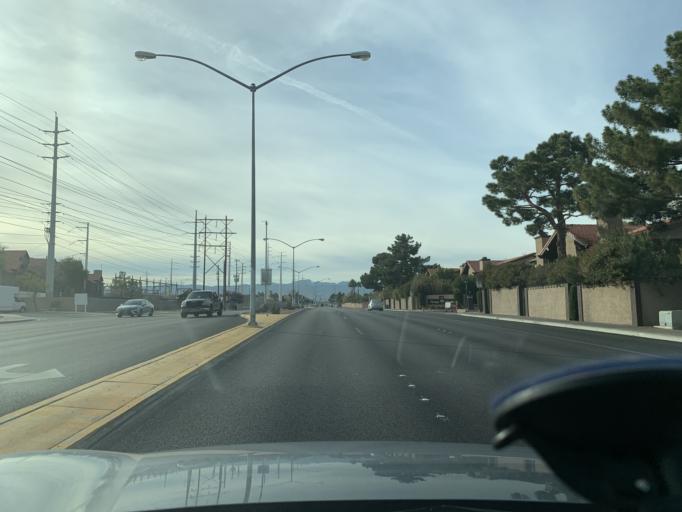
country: US
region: Nevada
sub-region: Clark County
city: Spring Valley
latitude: 36.1154
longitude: -115.2104
